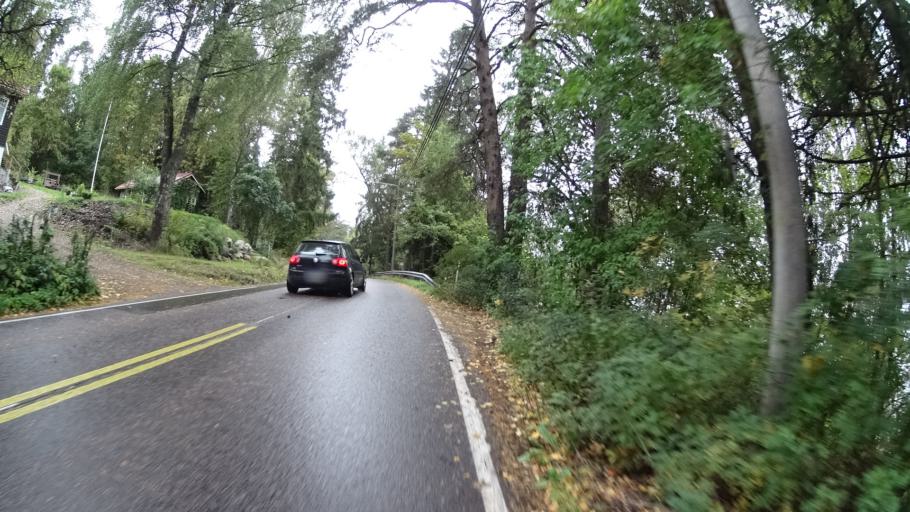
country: FI
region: Uusimaa
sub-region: Helsinki
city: Espoo
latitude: 60.2647
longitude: 24.6559
